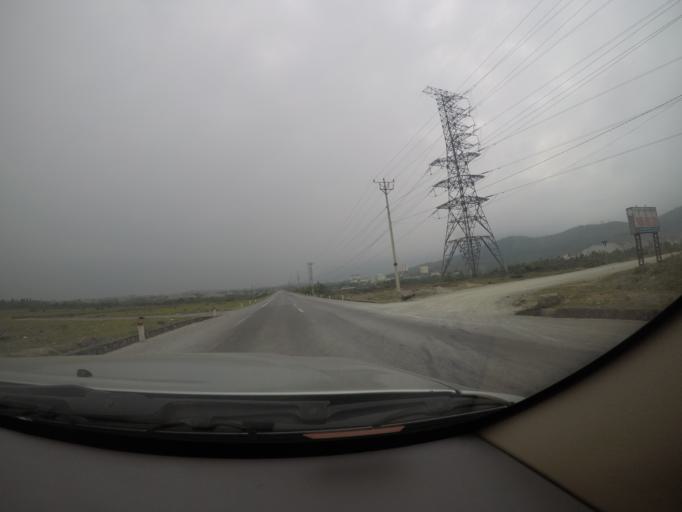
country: VN
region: Ha Tinh
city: Ky Anh
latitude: 18.0048
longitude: 106.4267
